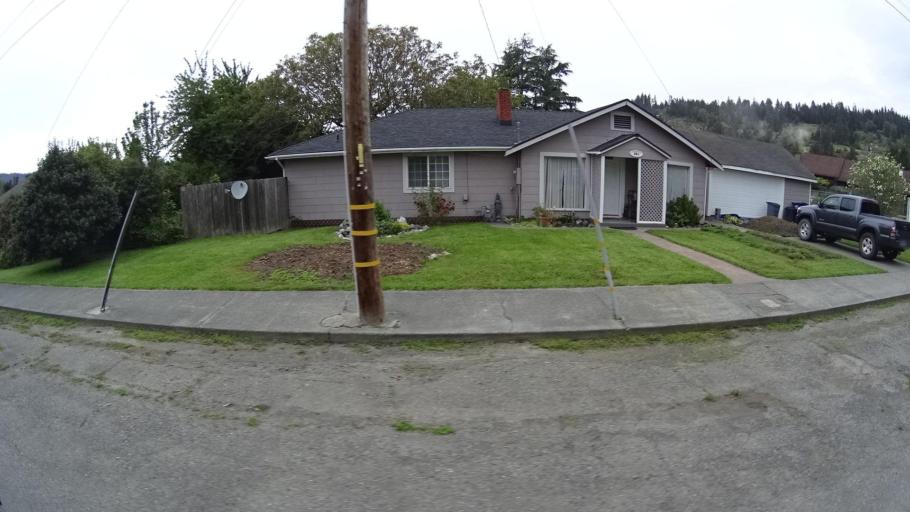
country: US
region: California
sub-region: Humboldt County
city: Blue Lake
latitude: 40.8824
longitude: -123.9878
